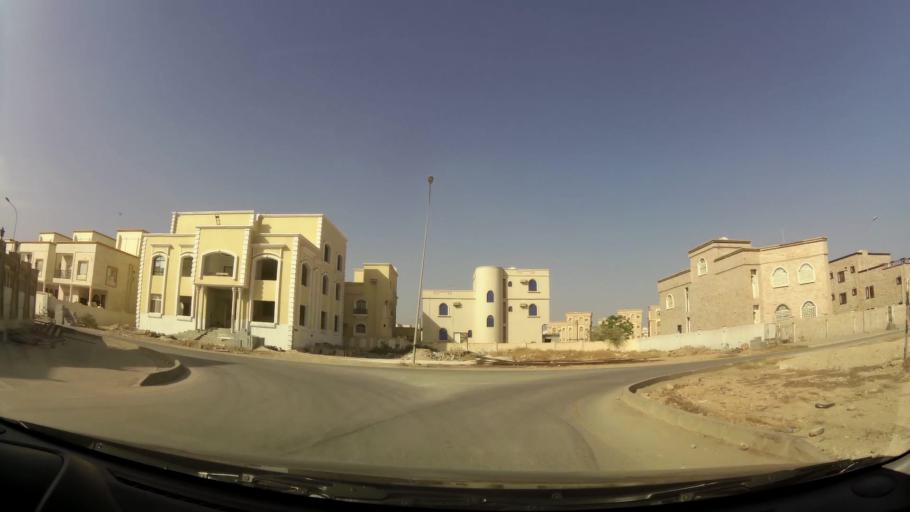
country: OM
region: Zufar
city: Salalah
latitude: 17.0083
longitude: 54.0244
